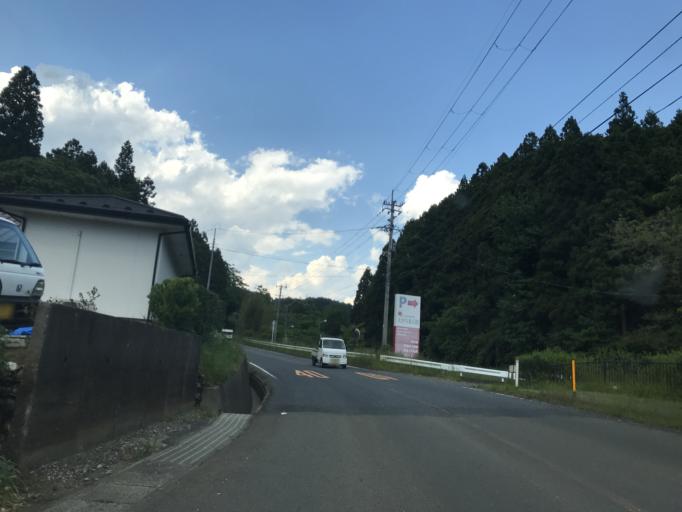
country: JP
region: Miyagi
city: Wakuya
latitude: 38.5583
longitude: 141.1363
